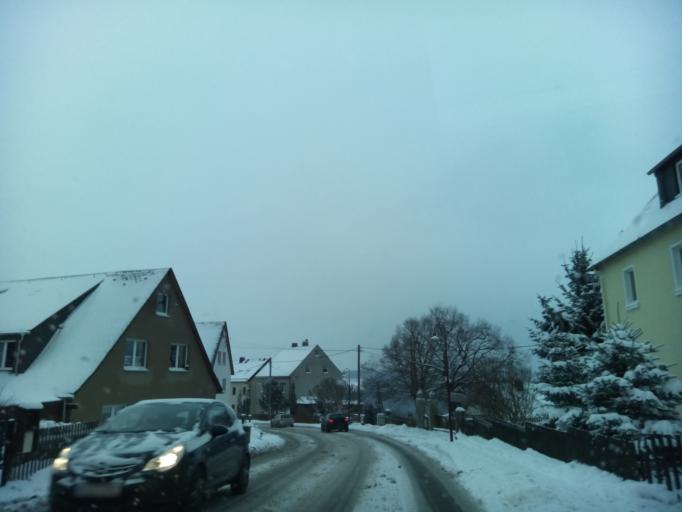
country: DE
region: Saxony
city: Lengefeld
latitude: 50.7407
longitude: 13.1763
